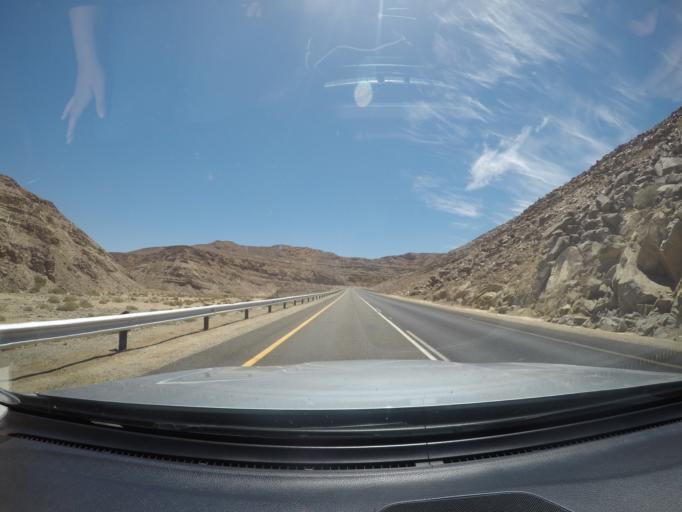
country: ZA
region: Northern Cape
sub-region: Namakwa District Municipality
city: Springbok
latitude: -28.7911
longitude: 17.6497
